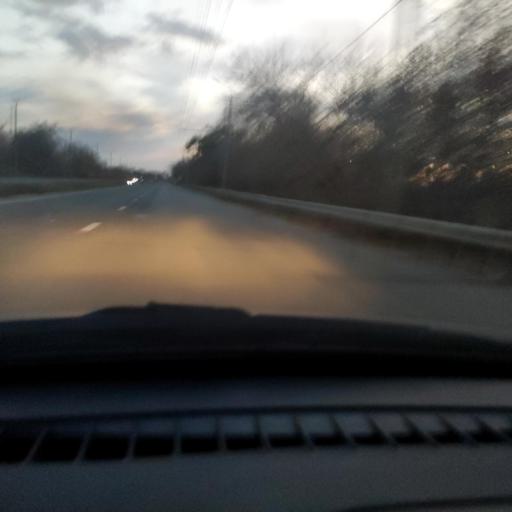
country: RU
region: Samara
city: Zhigulevsk
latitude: 53.5385
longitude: 49.5653
